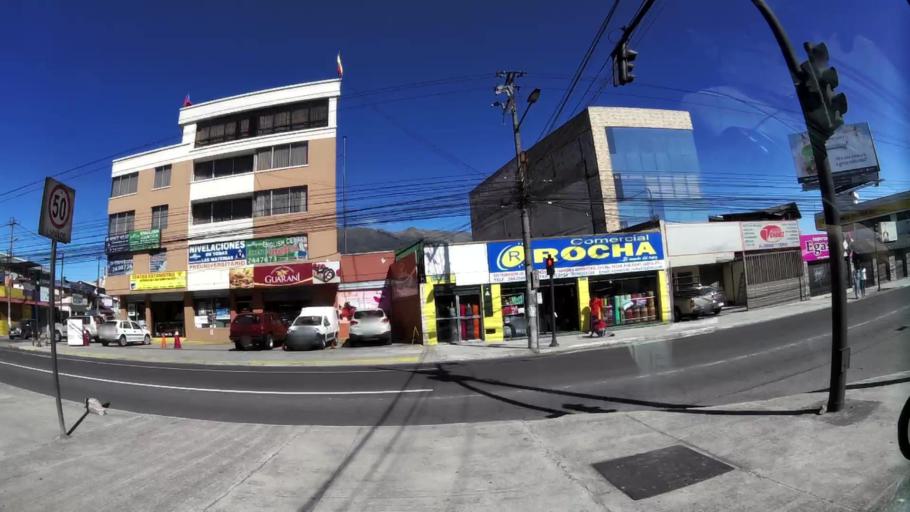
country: EC
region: Pichincha
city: Quito
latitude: -0.1574
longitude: -78.4770
